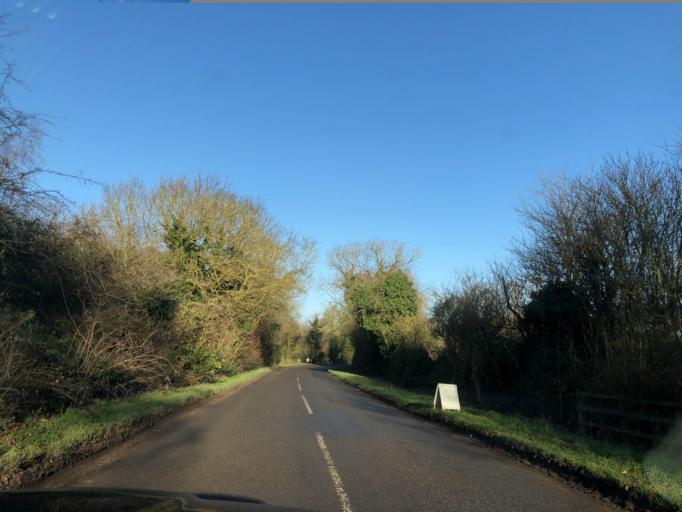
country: GB
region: England
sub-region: Warwickshire
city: Harbury
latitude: 52.2035
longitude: -1.5025
